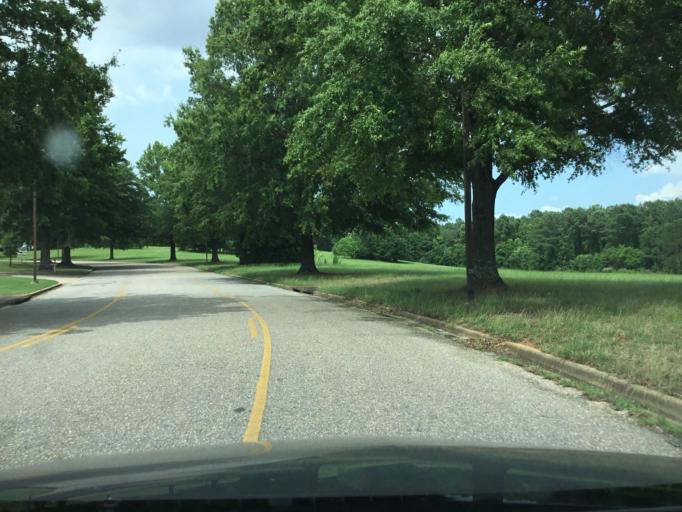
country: US
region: Alabama
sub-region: Montgomery County
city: Pike Road
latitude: 32.3703
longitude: -86.1281
